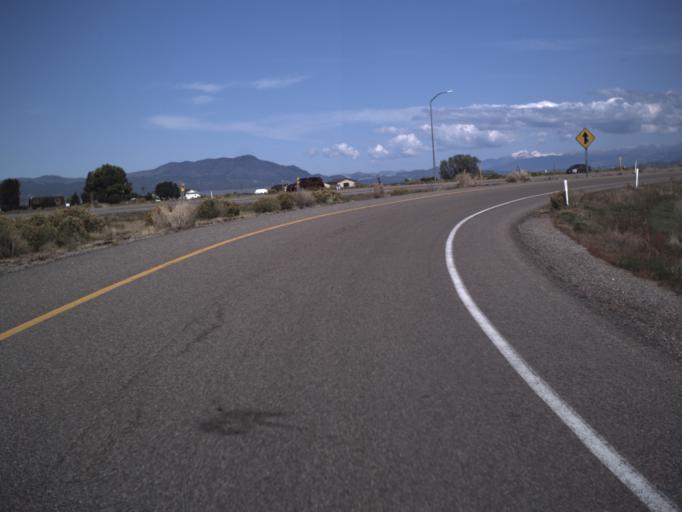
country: US
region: Utah
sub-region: Iron County
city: Parowan
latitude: 37.8394
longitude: -112.8665
